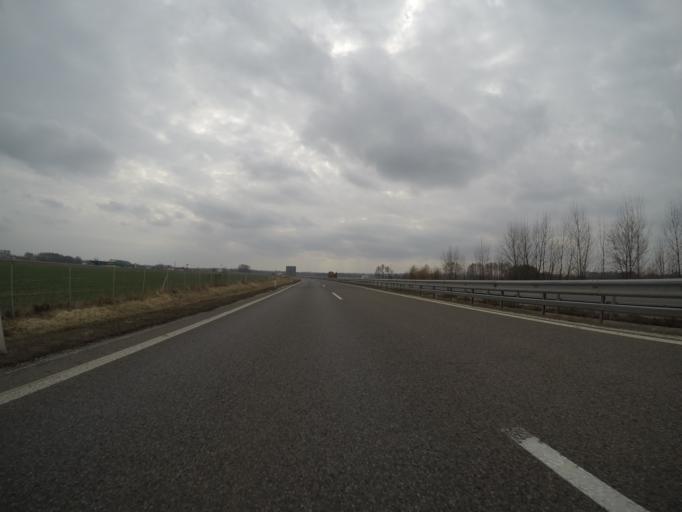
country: SI
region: Lendava-Lendva
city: Lendava
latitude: 46.5463
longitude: 16.4424
